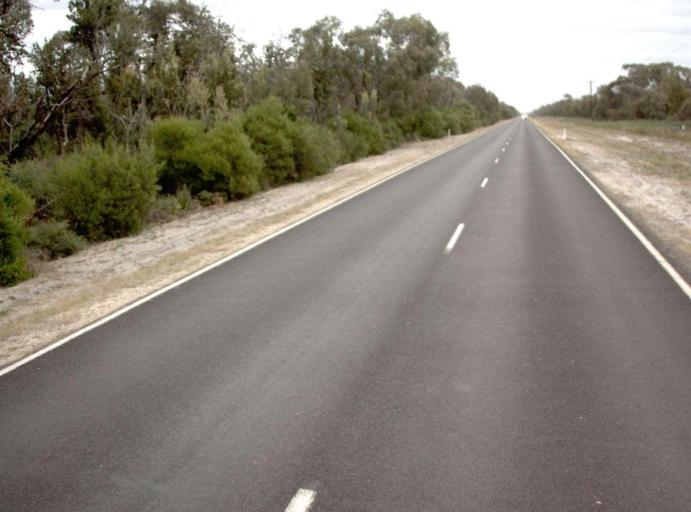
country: AU
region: Victoria
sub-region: East Gippsland
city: Bairnsdale
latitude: -38.0667
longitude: 147.5547
